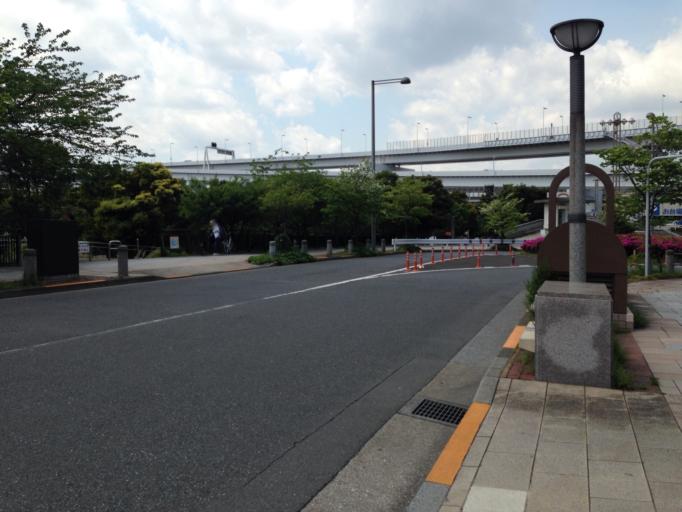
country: JP
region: Tokyo
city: Tokyo
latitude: 35.6347
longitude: 139.7760
